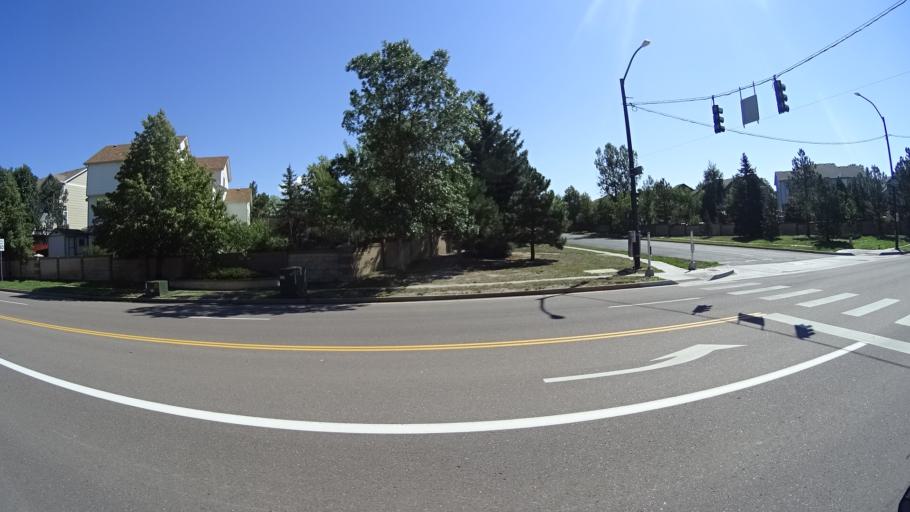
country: US
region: Colorado
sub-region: El Paso County
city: Black Forest
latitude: 38.9622
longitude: -104.7715
